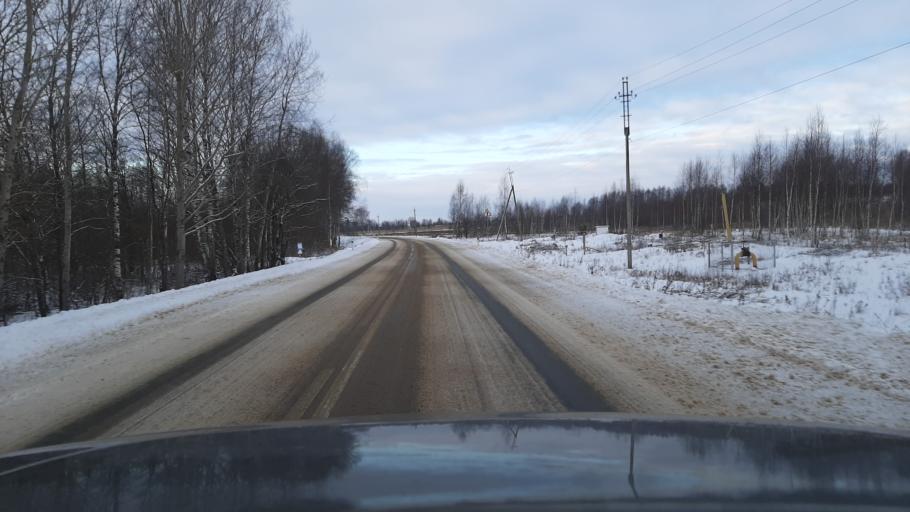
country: RU
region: Kostroma
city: Nerekhta
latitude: 57.4724
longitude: 40.6572
